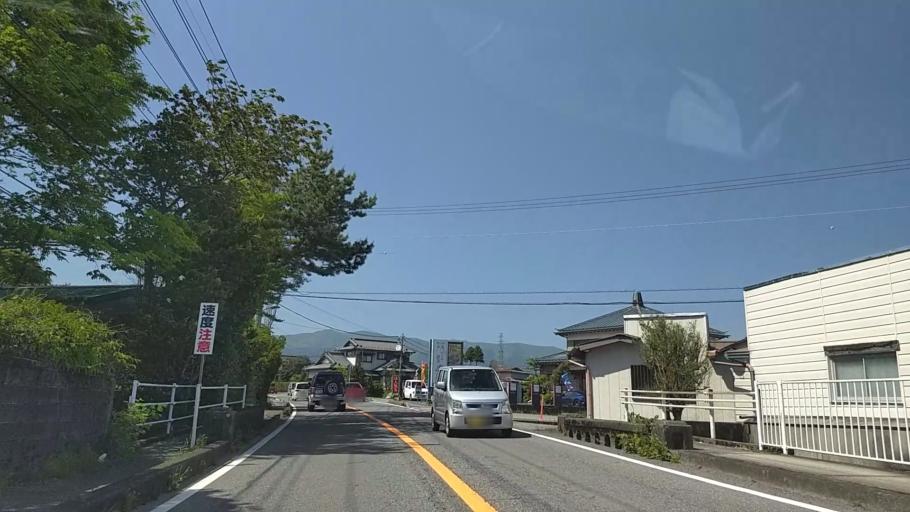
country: JP
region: Shizuoka
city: Gotemba
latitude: 35.3121
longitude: 138.9219
